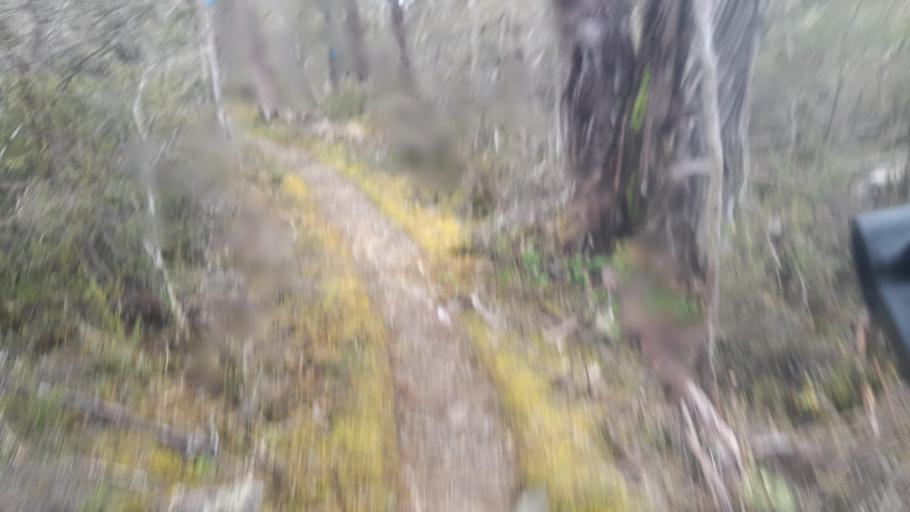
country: NZ
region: Tasman
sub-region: Tasman District
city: Wakefield
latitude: -41.7779
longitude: 172.8132
